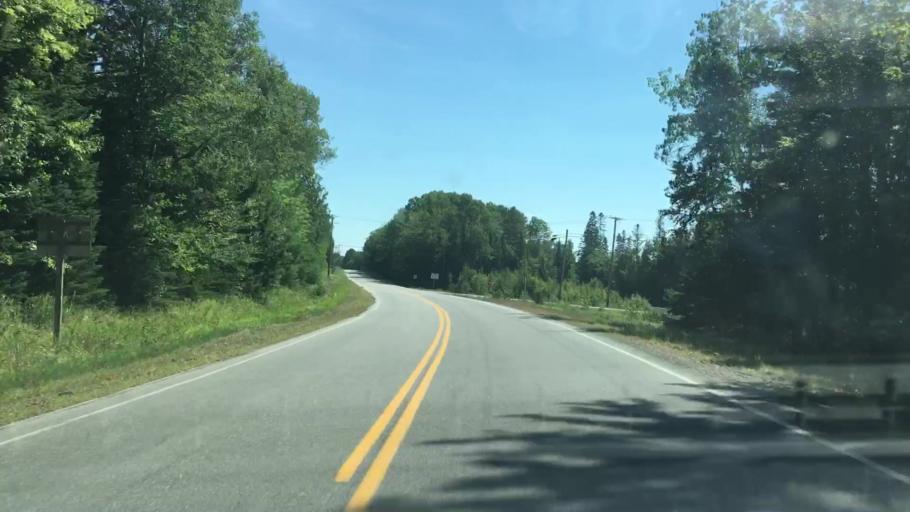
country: US
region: Maine
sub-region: Piscataquis County
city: Milo
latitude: 45.2001
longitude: -68.9064
